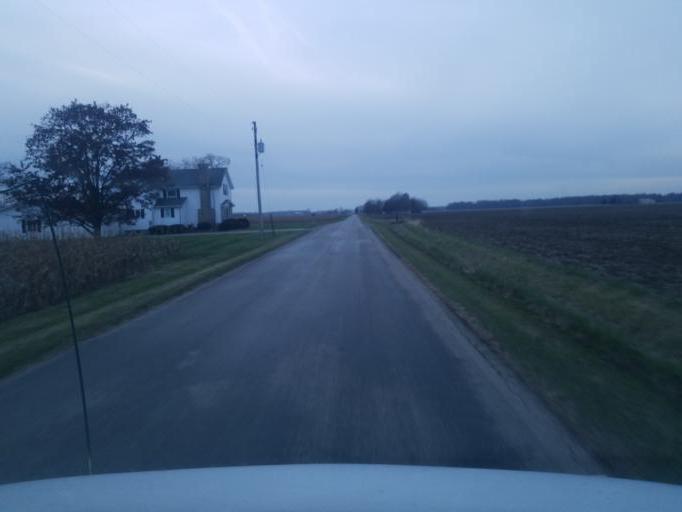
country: US
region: Indiana
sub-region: Adams County
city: Decatur
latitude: 40.7880
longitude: -84.9855
